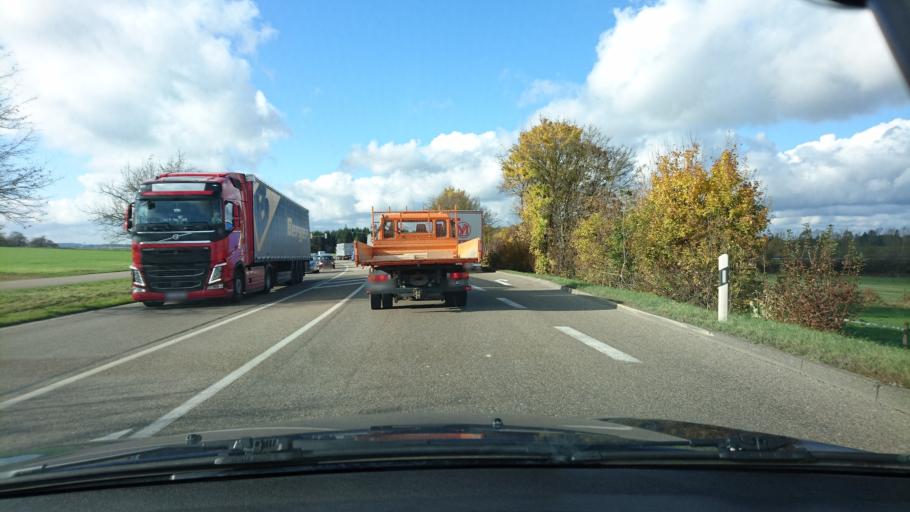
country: DE
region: Baden-Wuerttemberg
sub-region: Regierungsbezirk Stuttgart
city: Westhausen
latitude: 48.8881
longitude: 10.1520
